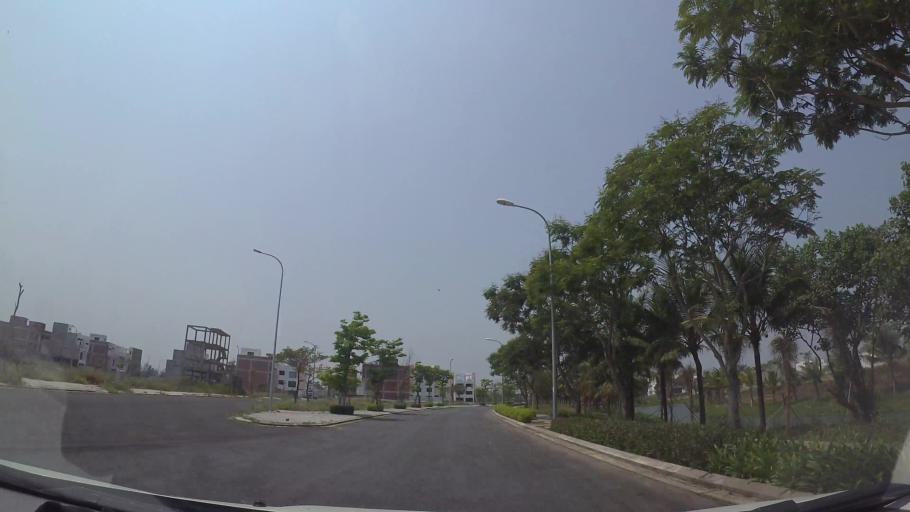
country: VN
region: Da Nang
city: Ngu Hanh Son
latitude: 15.9732
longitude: 108.2625
